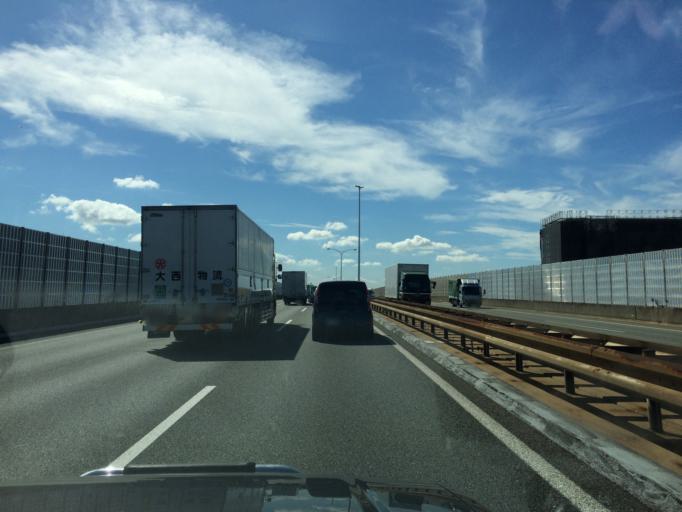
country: JP
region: Osaka
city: Yao
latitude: 34.6656
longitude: 135.5982
